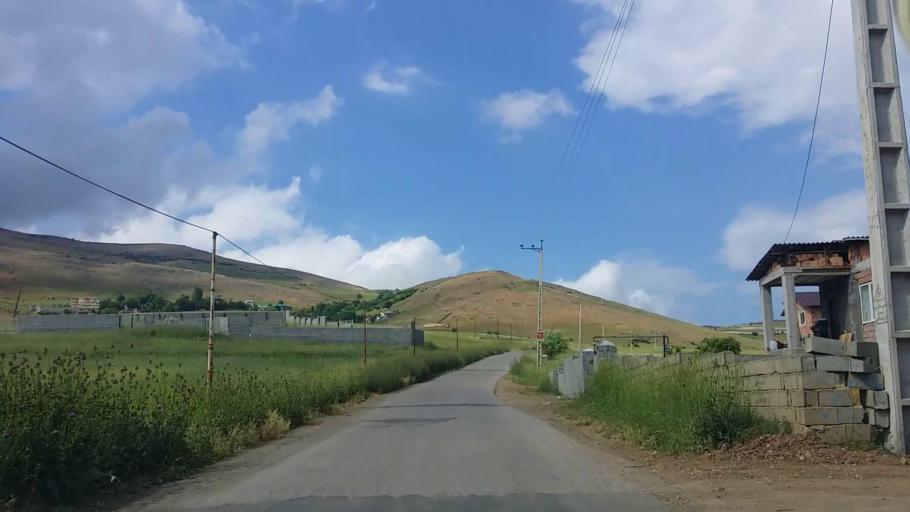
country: IR
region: Mazandaran
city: Chalus
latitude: 36.5221
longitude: 51.2616
